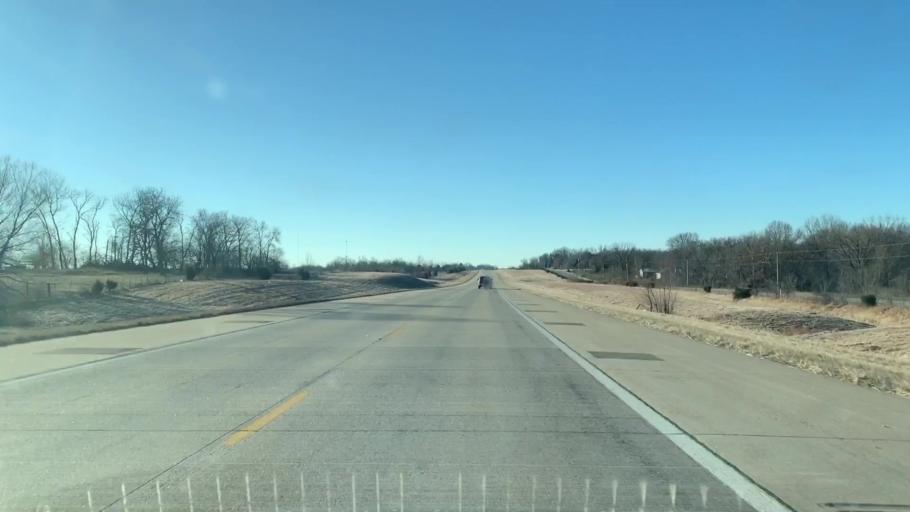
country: US
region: Kansas
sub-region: Crawford County
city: Arma
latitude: 37.5710
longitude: -94.7046
